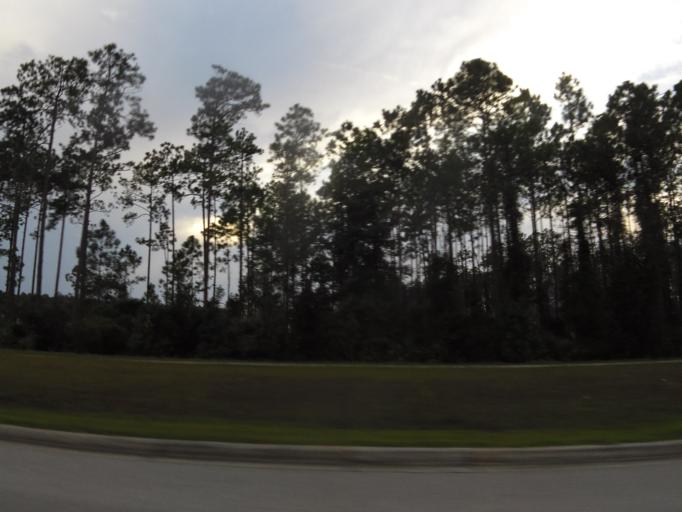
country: US
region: Florida
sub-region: Saint Johns County
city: Fruit Cove
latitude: 30.0663
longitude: -81.6041
